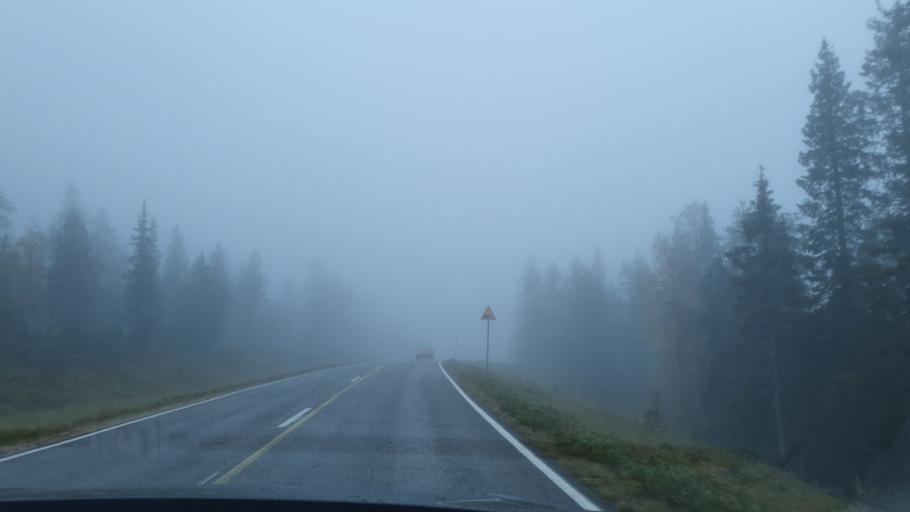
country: FI
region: Lapland
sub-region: Tunturi-Lappi
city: Kolari
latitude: 67.5477
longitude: 24.2127
